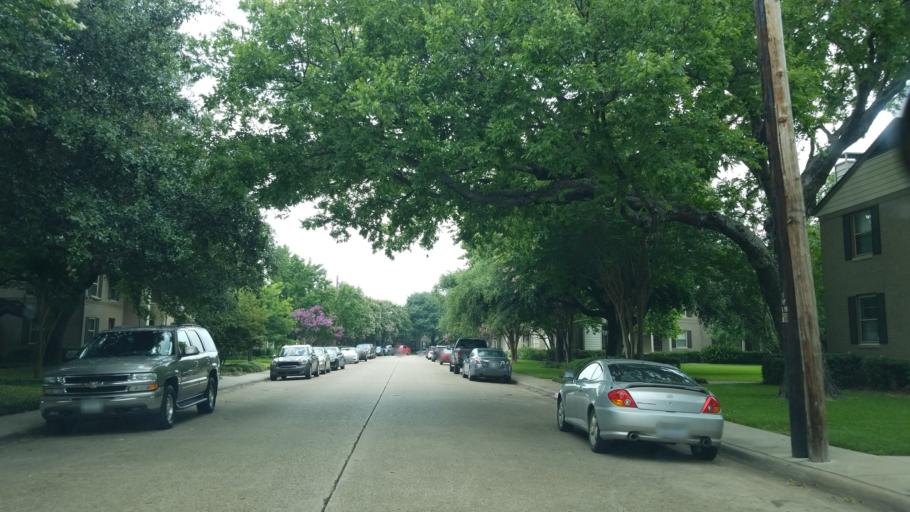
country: US
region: Texas
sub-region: Dallas County
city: University Park
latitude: 32.8346
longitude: -96.8253
